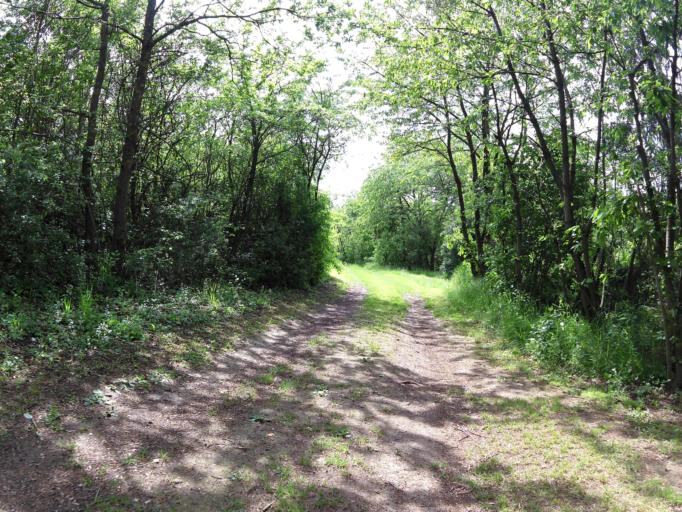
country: DE
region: Bavaria
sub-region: Regierungsbezirk Unterfranken
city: Eibelstadt
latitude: 49.7200
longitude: 10.0122
